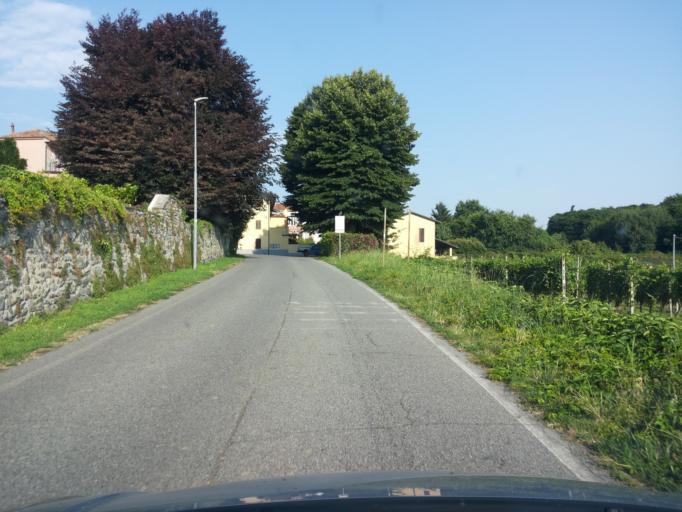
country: IT
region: Piedmont
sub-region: Provincia di Biella
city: Roppolo
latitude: 45.4212
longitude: 8.0650
